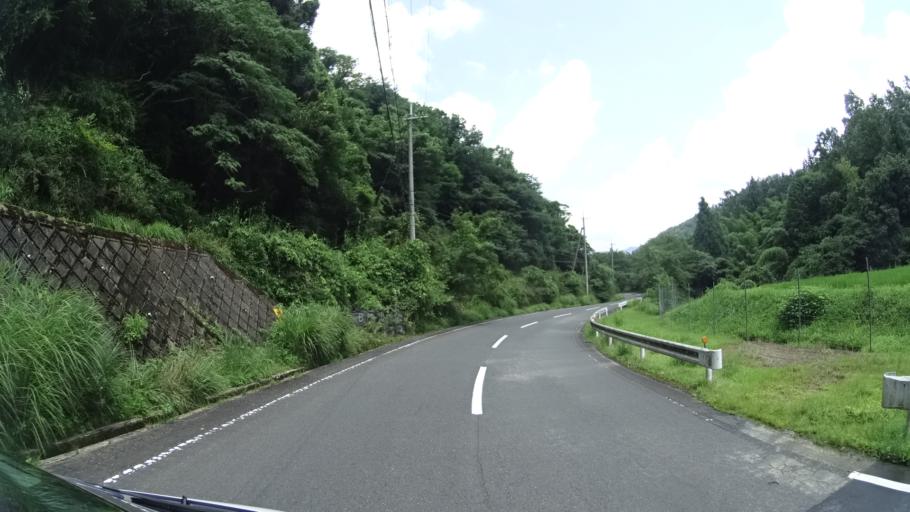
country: JP
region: Kyoto
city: Ayabe
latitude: 35.1902
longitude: 135.2448
